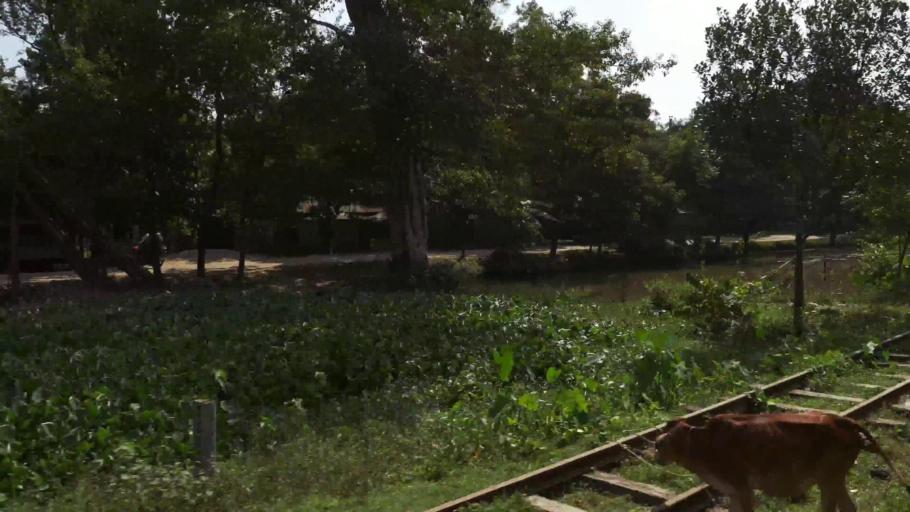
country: BD
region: Dhaka
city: Gafargaon
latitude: 24.1903
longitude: 90.4770
